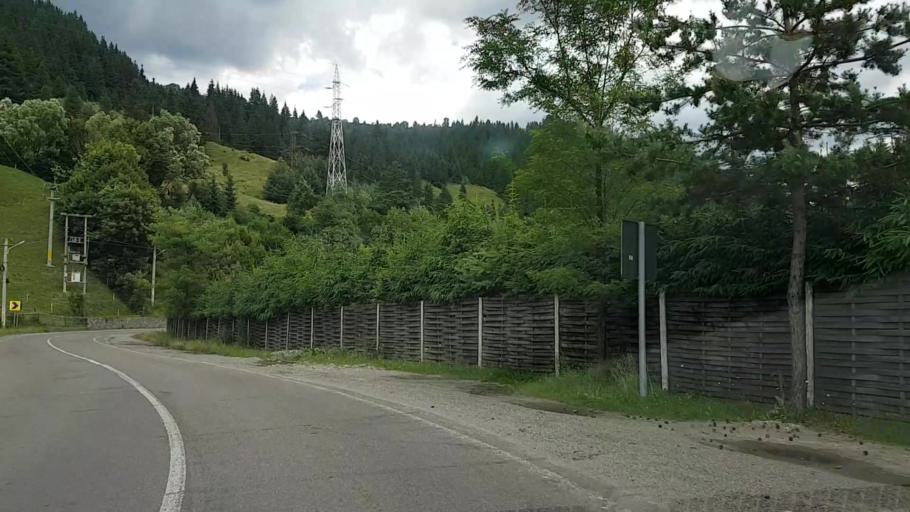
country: RO
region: Suceava
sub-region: Comuna Brosteni
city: Brosteni
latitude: 47.2331
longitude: 25.7243
